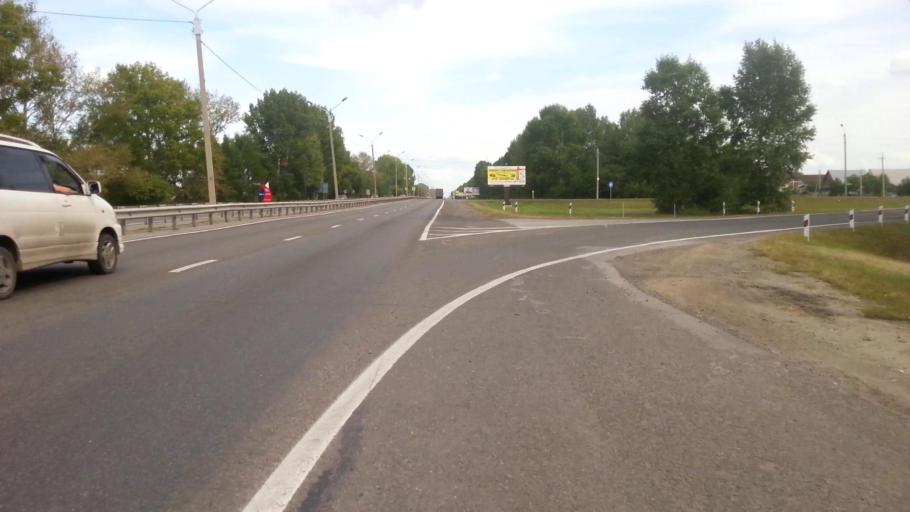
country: RU
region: Altai Krai
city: Vlasikha
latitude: 53.3535
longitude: 83.5550
